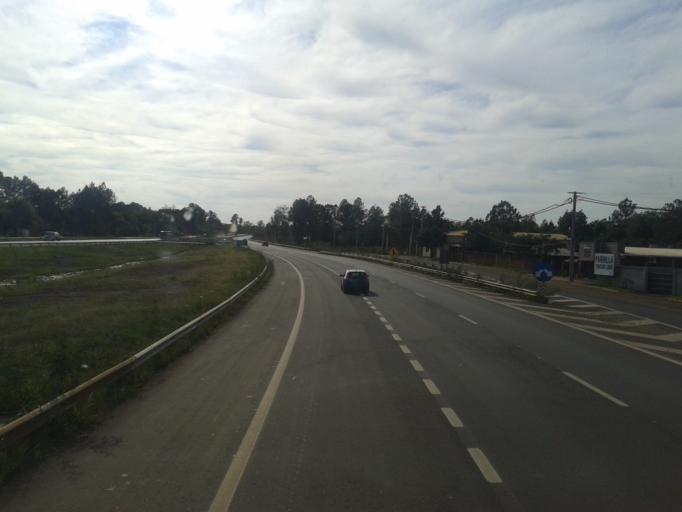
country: AR
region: Misiones
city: Garupa
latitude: -27.4666
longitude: -55.8019
